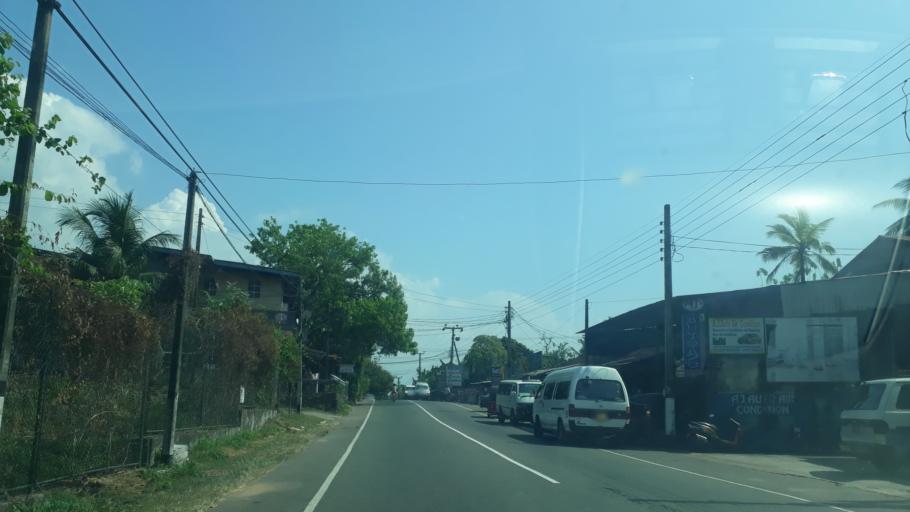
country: LK
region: Western
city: Gampaha
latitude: 7.0801
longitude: 80.0121
